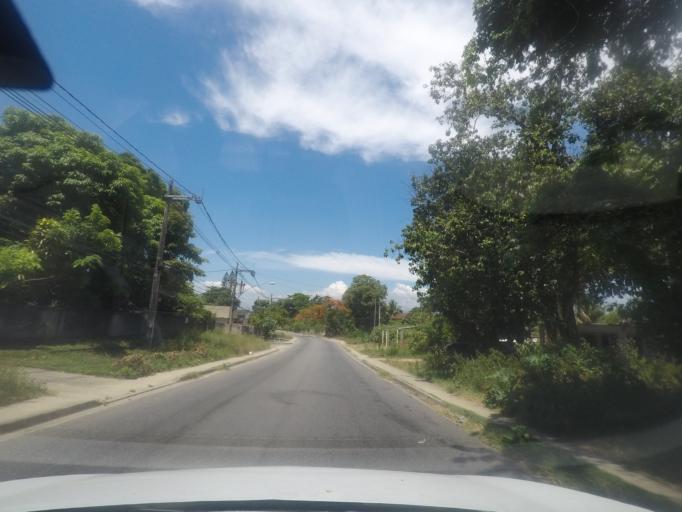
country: BR
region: Rio de Janeiro
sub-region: Itaguai
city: Itaguai
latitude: -22.9806
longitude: -43.6831
